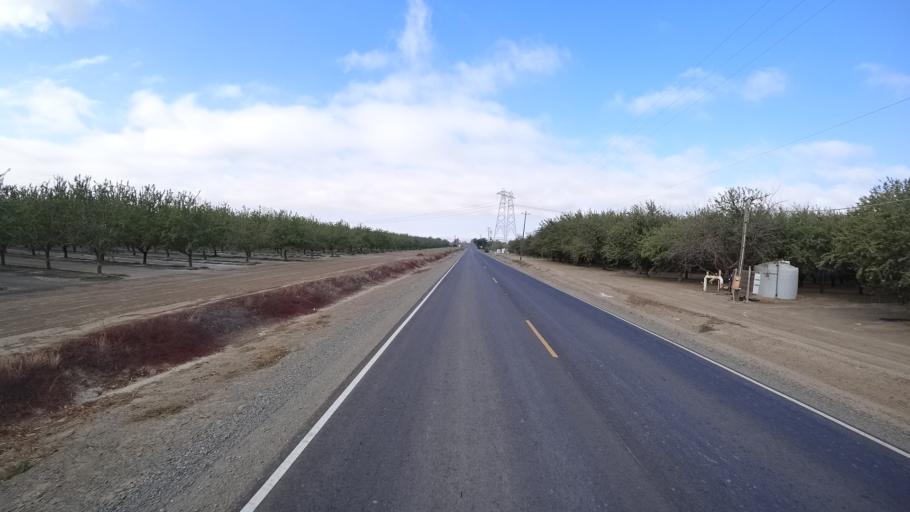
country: US
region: California
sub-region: Yolo County
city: Dunnigan
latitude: 38.7942
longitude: -121.8724
